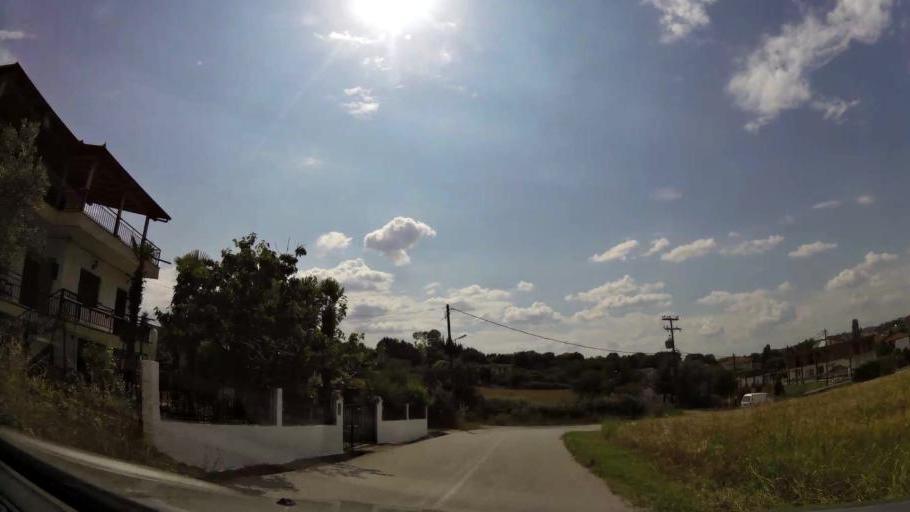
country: GR
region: Central Macedonia
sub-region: Nomos Pierias
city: Makrygialos
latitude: 40.4086
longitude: 22.6090
